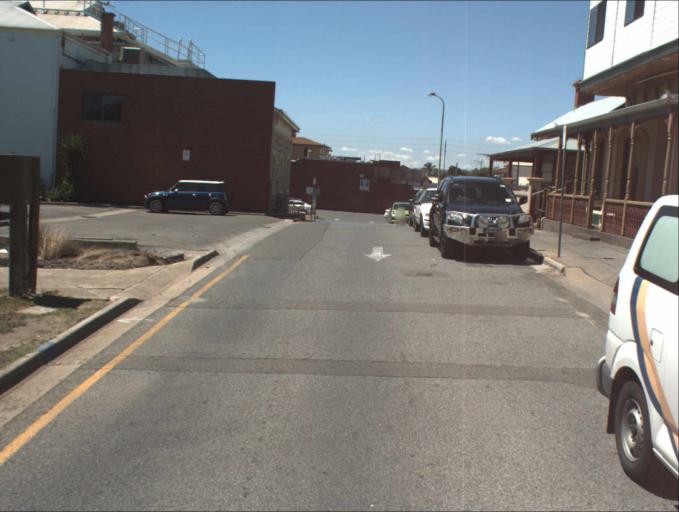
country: AU
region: South Australia
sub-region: Port Adelaide Enfield
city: Birkenhead
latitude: -34.8390
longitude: 138.4806
